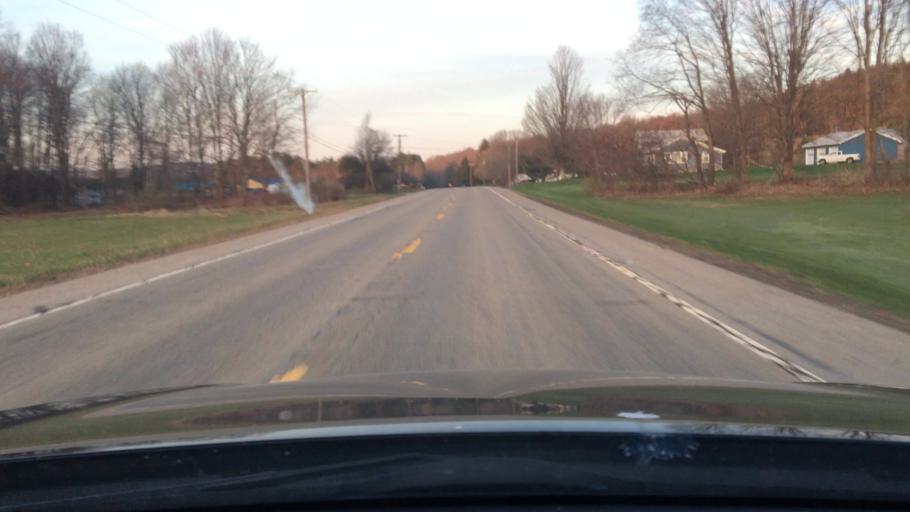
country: US
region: New York
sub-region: Cattaraugus County
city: Randolph
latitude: 42.1784
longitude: -78.9275
